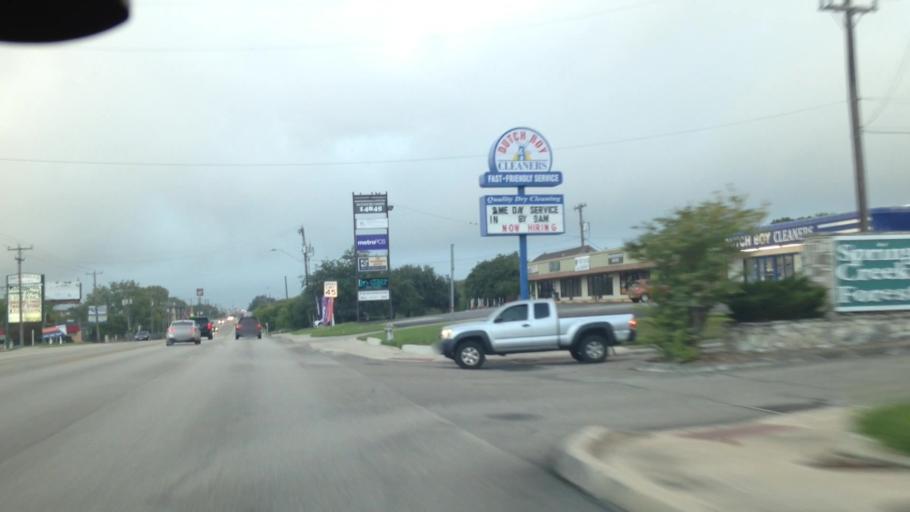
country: US
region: Texas
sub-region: Bexar County
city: Live Oak
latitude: 29.5772
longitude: -98.3740
